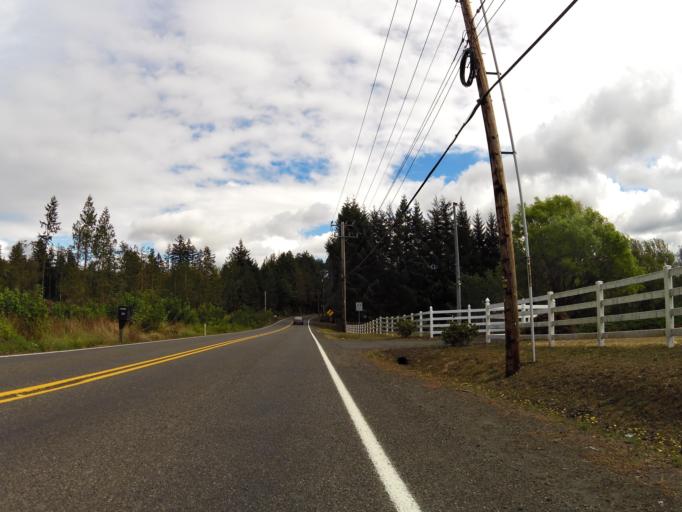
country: US
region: Washington
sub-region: Mason County
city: Shelton
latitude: 47.1810
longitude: -123.0951
